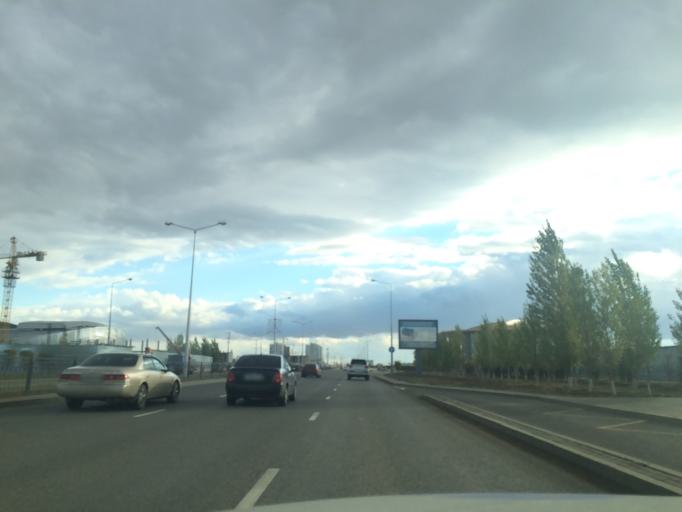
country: KZ
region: Astana Qalasy
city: Astana
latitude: 51.1143
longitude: 71.3998
